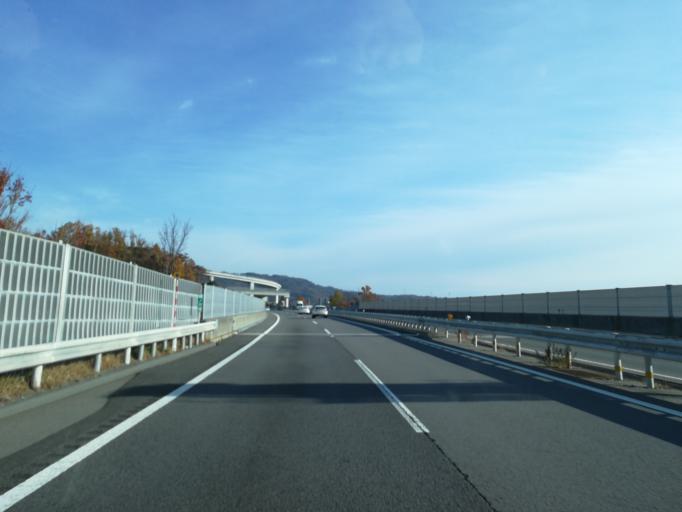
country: JP
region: Nagano
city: Ueda
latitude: 36.4108
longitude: 138.2877
